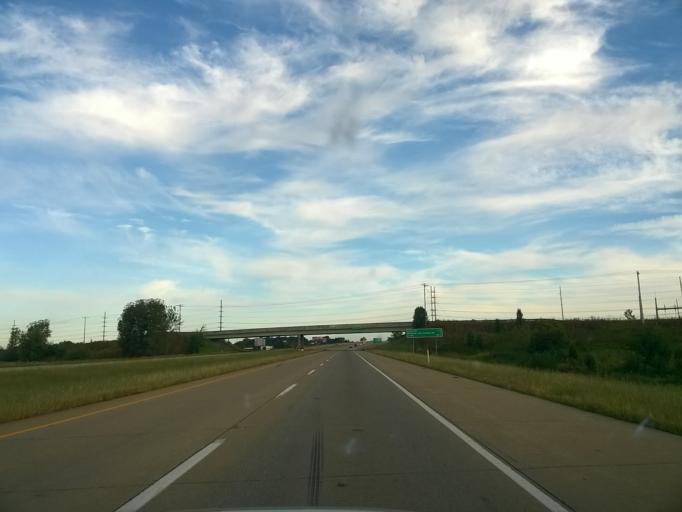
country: US
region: Indiana
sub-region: Vanderburgh County
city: Melody Hill
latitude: 37.9908
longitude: -87.4623
